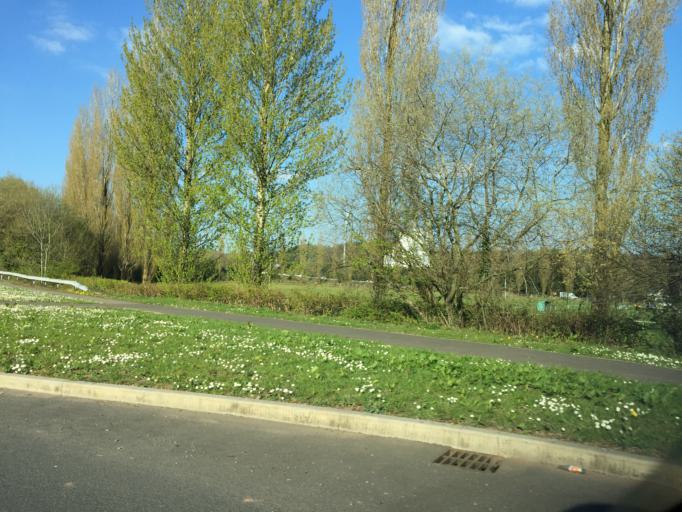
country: GB
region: Wales
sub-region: Torfaen County Borough
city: Cwmbran
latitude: 51.6705
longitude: -3.0217
